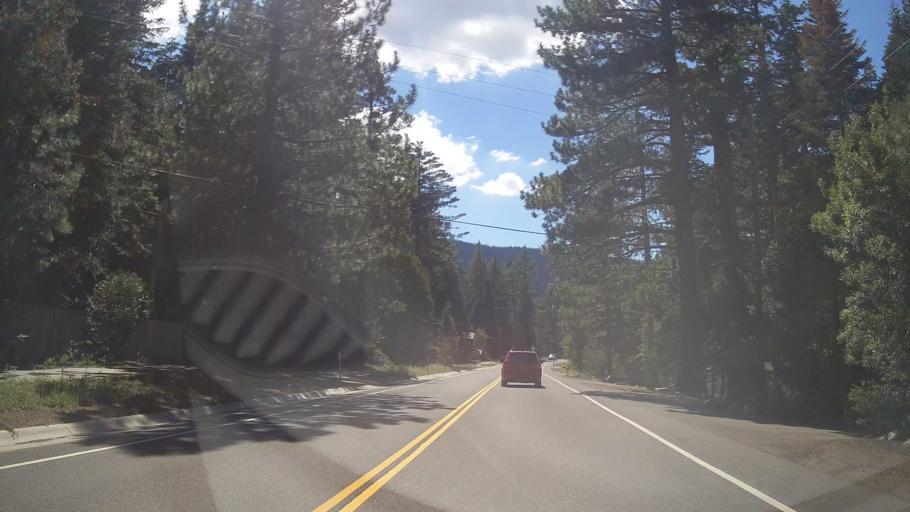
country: US
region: California
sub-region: Placer County
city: Tahoma
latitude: 39.0685
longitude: -120.1317
